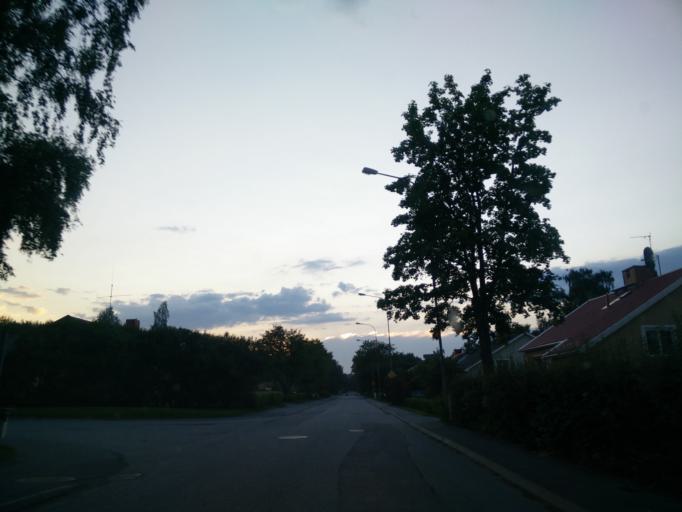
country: SE
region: Vaesternorrland
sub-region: Solleftea Kommun
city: Solleftea
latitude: 63.1651
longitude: 17.2686
